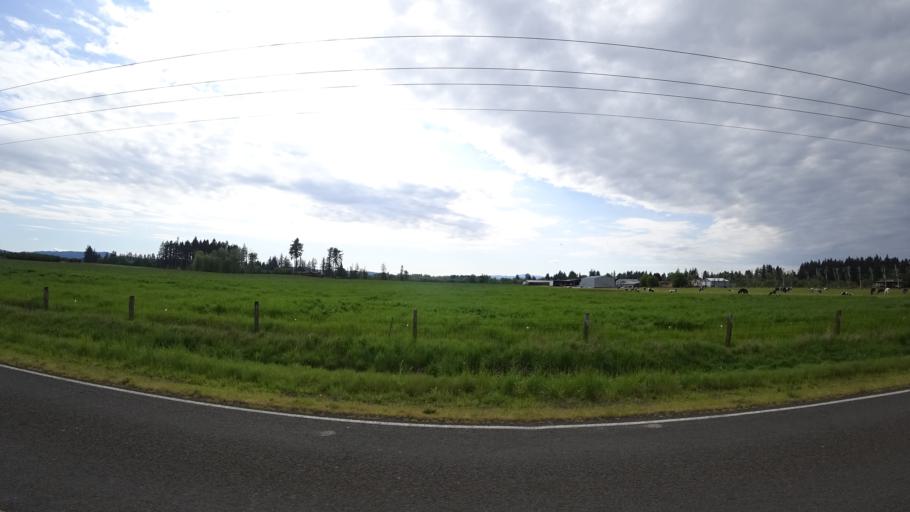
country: US
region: Oregon
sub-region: Washington County
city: Hillsboro
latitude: 45.4834
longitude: -122.9496
